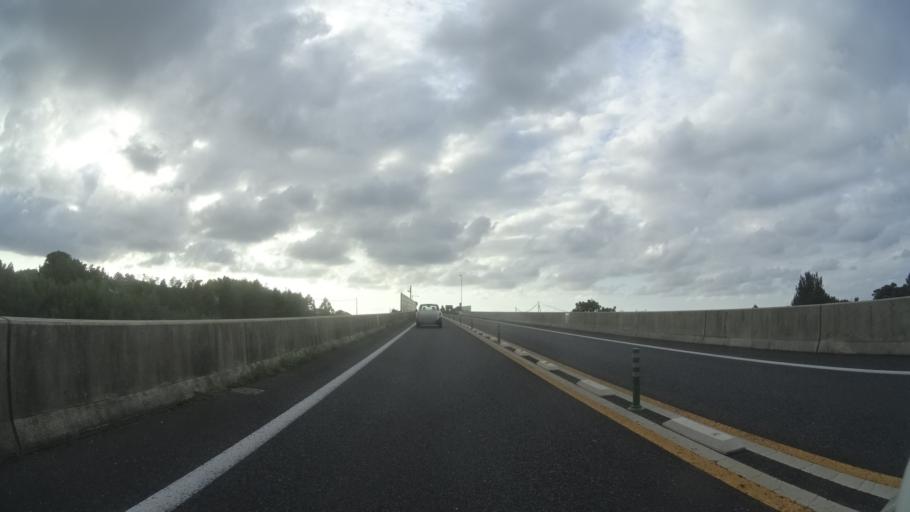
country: JP
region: Tottori
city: Kurayoshi
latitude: 35.5055
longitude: 133.6500
